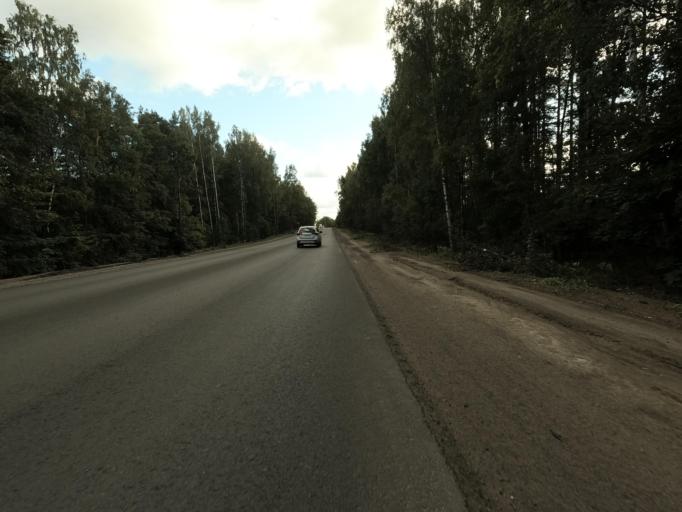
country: RU
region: Leningrad
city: Koltushi
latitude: 59.9522
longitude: 30.6567
